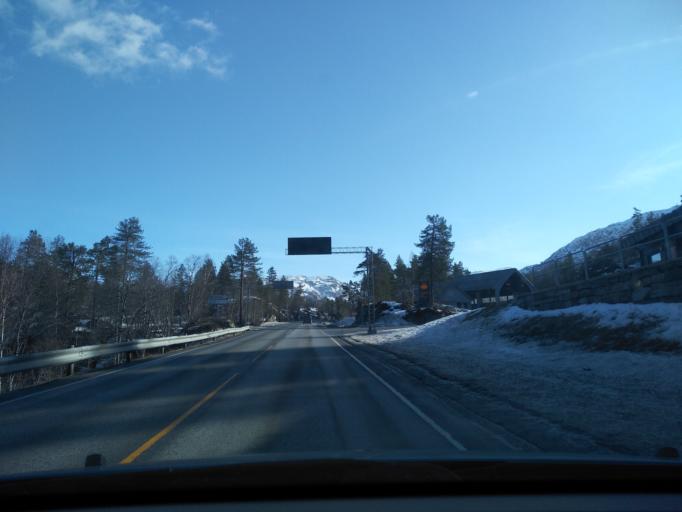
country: NO
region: Hordaland
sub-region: Odda
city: Odda
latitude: 59.9057
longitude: 6.6176
